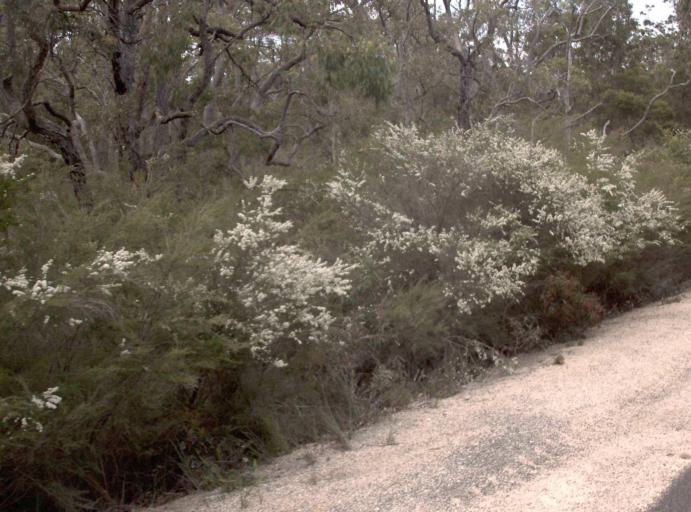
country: AU
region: New South Wales
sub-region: Bega Valley
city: Eden
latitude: -37.4526
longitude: 149.6186
